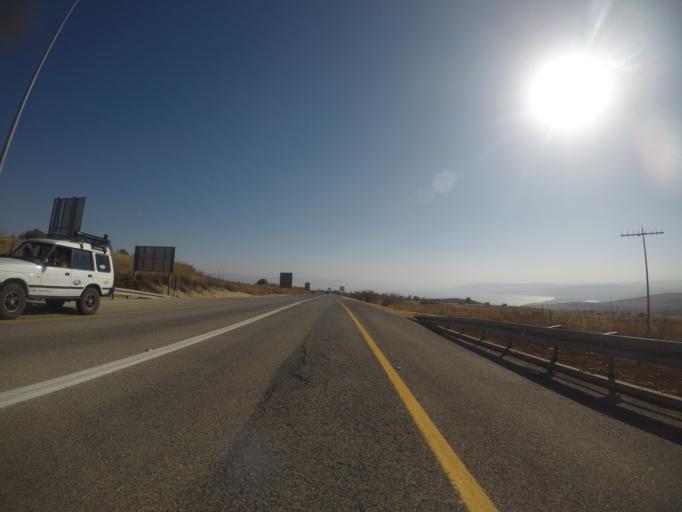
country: IL
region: Northern District
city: Rosh Pinna
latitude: 32.9116
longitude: 35.5456
